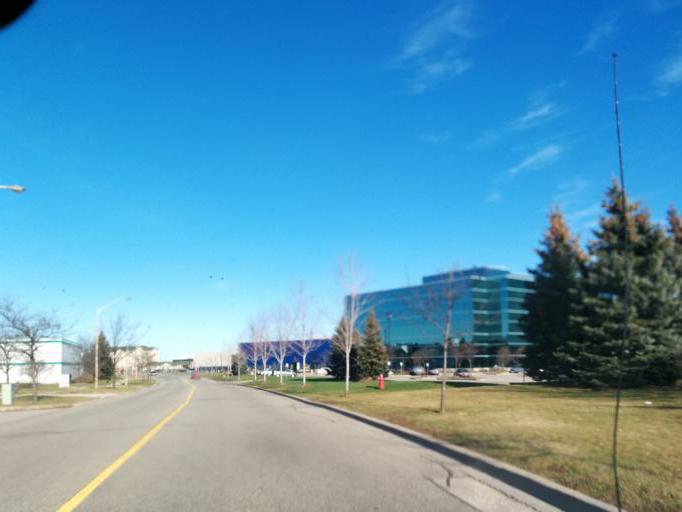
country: CA
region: Ontario
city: Oakville
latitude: 43.5074
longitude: -79.6719
